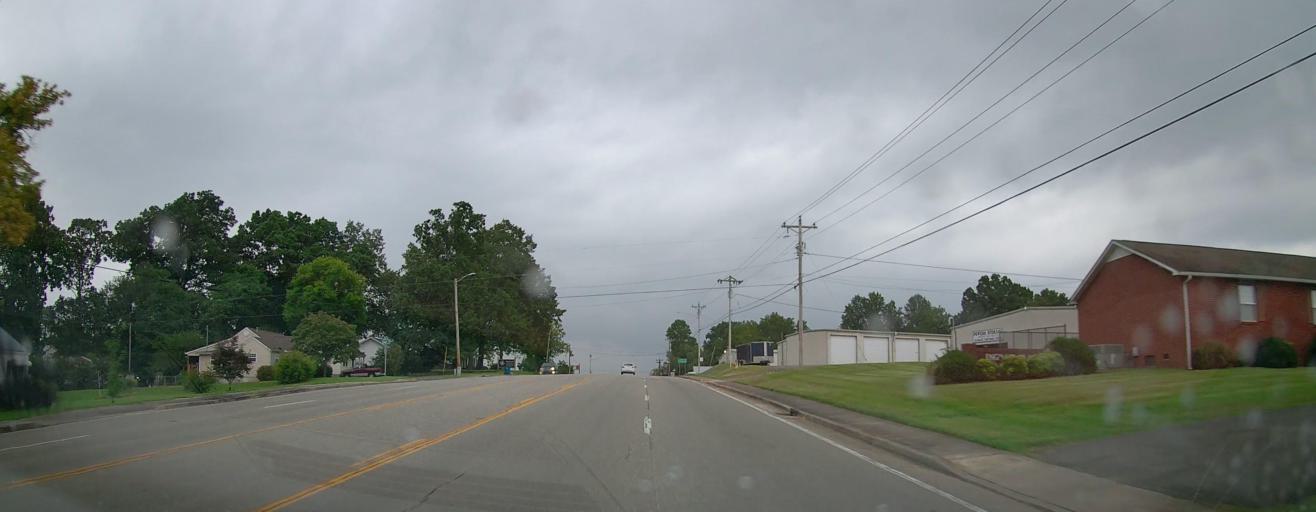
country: US
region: Tennessee
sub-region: Coffee County
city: Manchester
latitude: 35.4915
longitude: -86.0882
